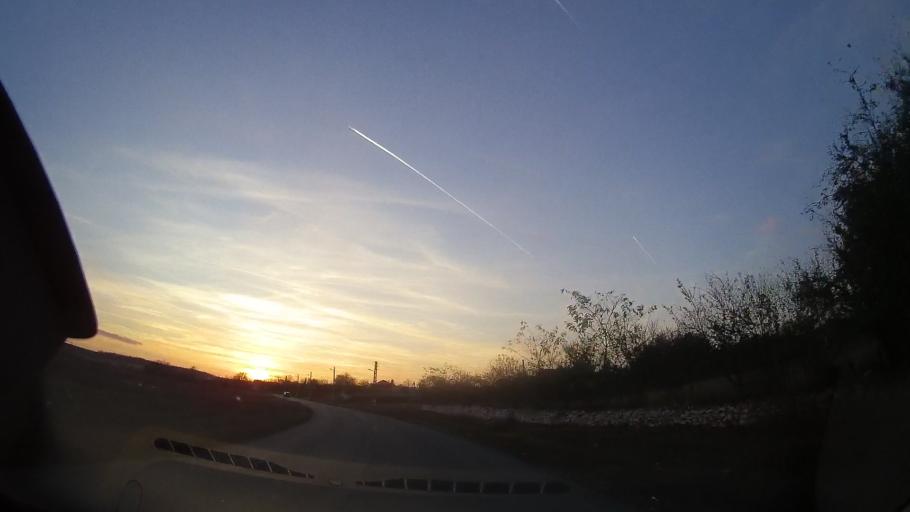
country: RO
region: Constanta
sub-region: Comuna Mereni
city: Mereni
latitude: 44.0164
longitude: 28.3206
